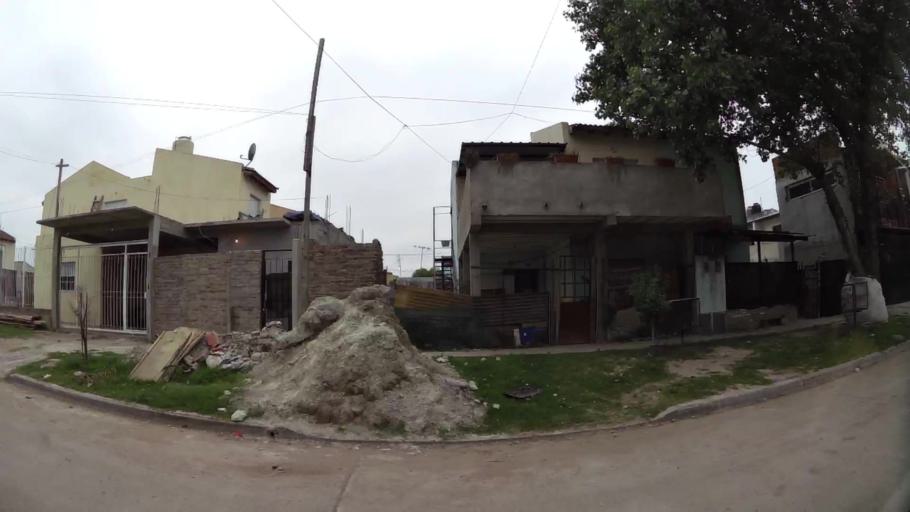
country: AR
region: Buenos Aires
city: San Justo
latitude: -34.6998
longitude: -58.5486
